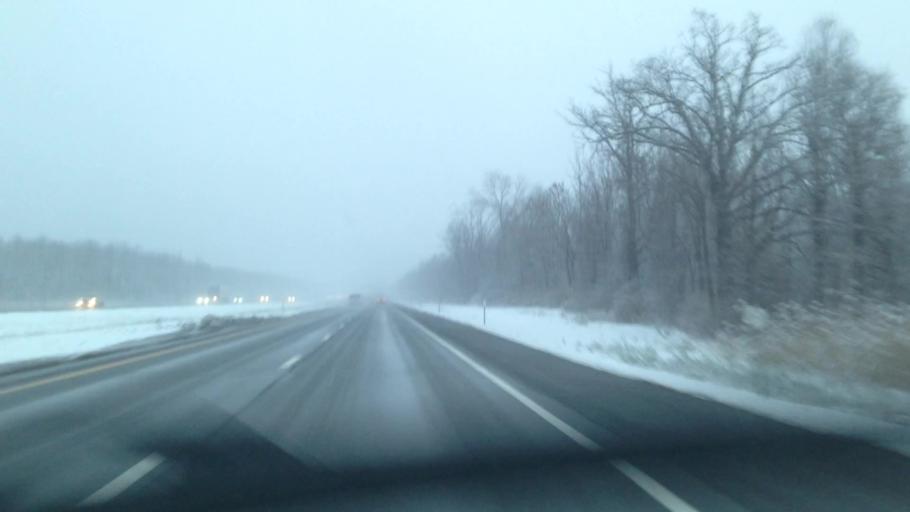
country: US
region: New York
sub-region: Madison County
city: Chittenango
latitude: 43.0939
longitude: -75.8205
